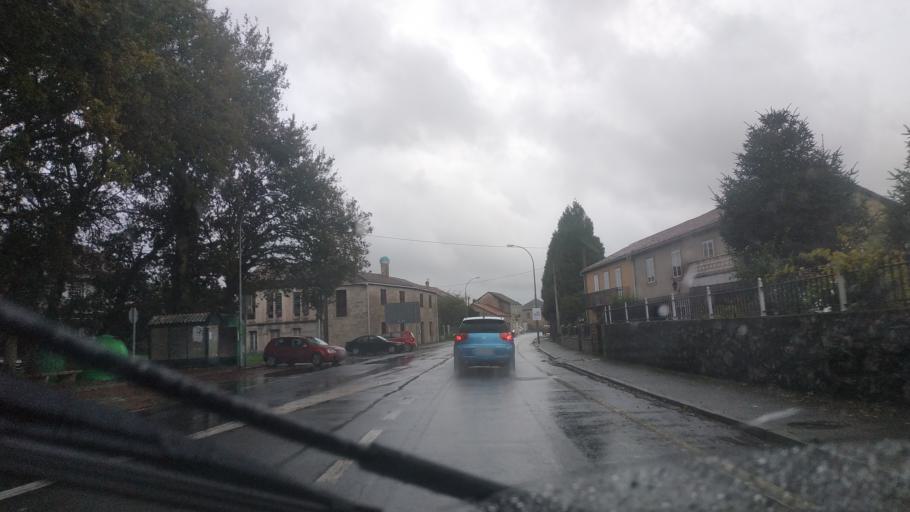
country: ES
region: Galicia
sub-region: Provincia da Coruna
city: Negreira
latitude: 42.9241
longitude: -8.7340
